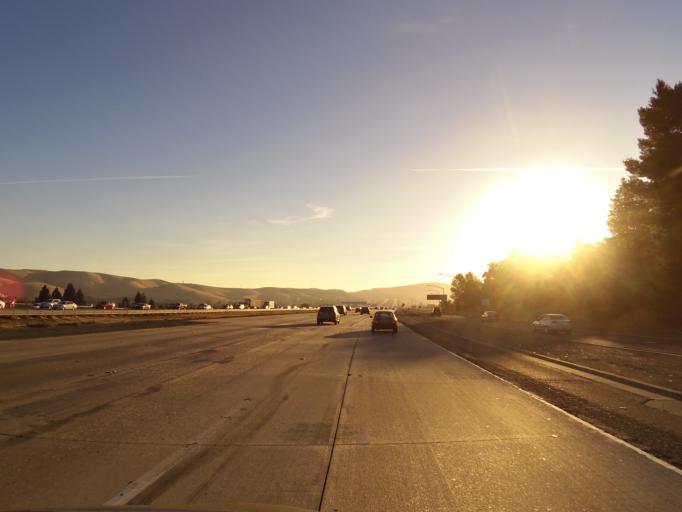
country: US
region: California
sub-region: Contra Costa County
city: Concord
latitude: 38.0082
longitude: -122.0293
